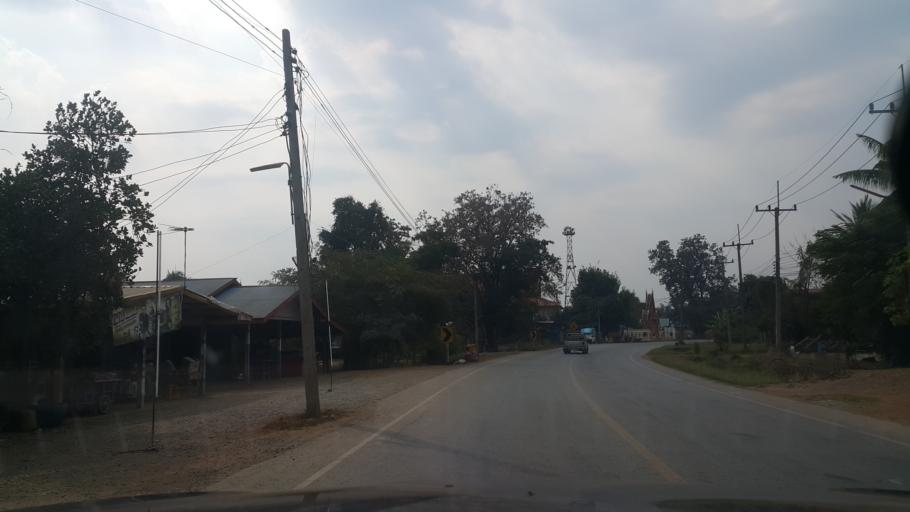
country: TH
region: Sukhothai
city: Si Samrong
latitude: 17.0893
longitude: 99.8838
